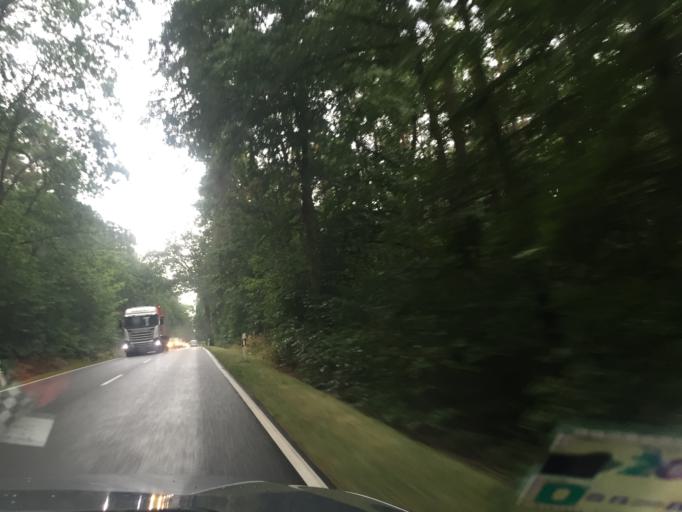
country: DE
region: Brandenburg
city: Liebenwalde
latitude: 52.8160
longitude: 13.4082
